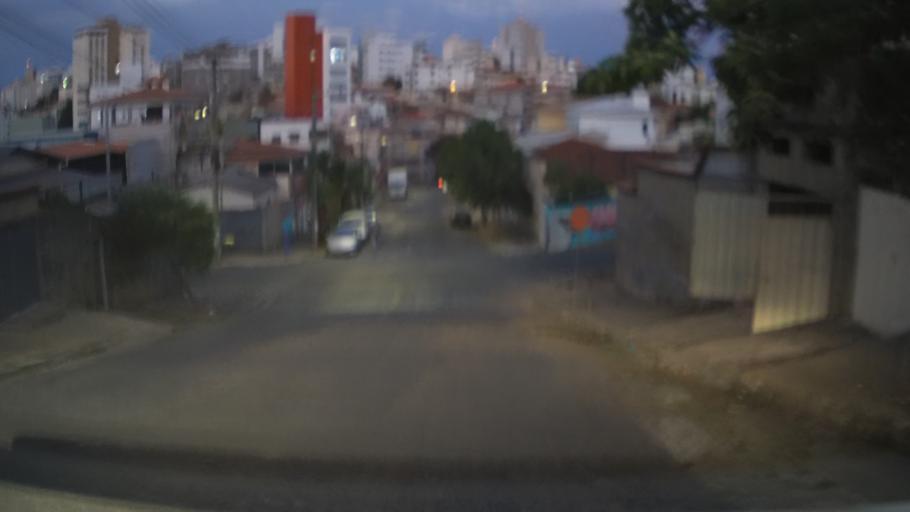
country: BR
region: Minas Gerais
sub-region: Belo Horizonte
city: Belo Horizonte
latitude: -19.9017
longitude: -43.9351
